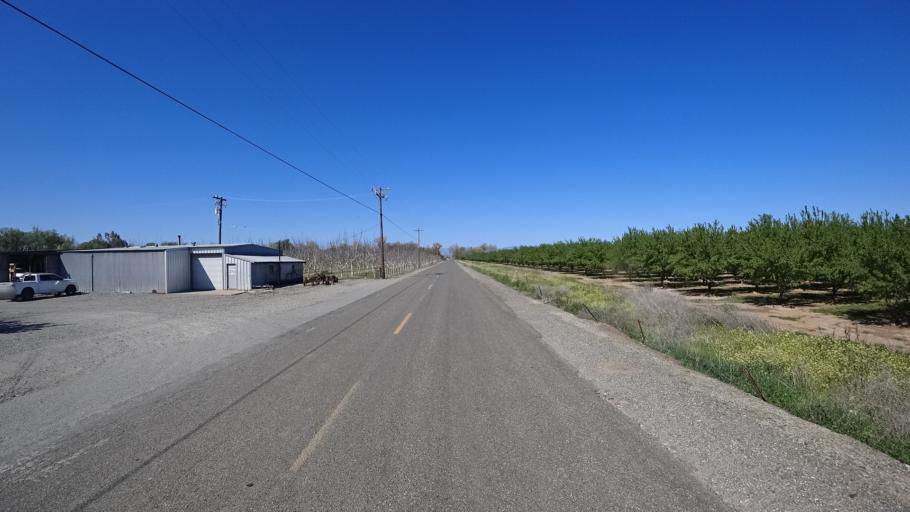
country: US
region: California
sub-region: Glenn County
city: Orland
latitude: 39.6971
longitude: -122.2194
